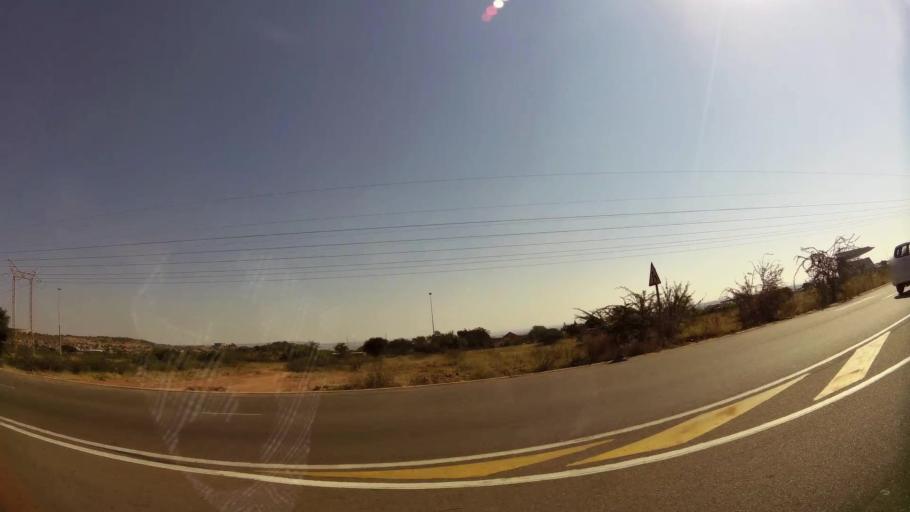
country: ZA
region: Gauteng
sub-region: City of Tshwane Metropolitan Municipality
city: Mabopane
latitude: -25.5229
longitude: 28.0881
